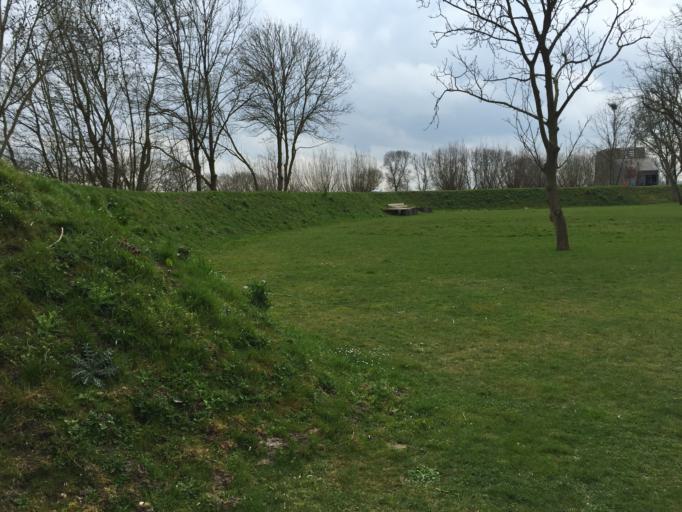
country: NL
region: Gelderland
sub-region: Gemeente Culemborg
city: Culemborg
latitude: 51.9598
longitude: 5.1911
